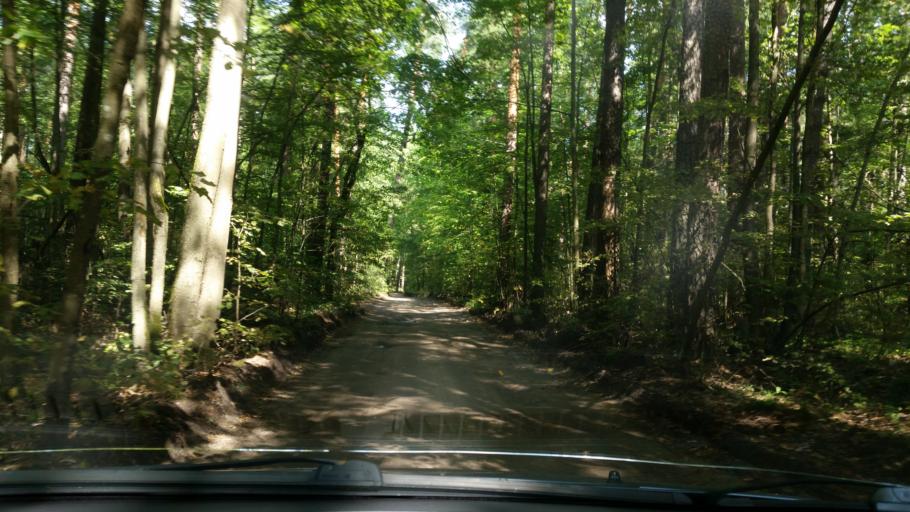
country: RU
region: Moskovskaya
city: Pushchino
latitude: 54.9094
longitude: 37.7159
